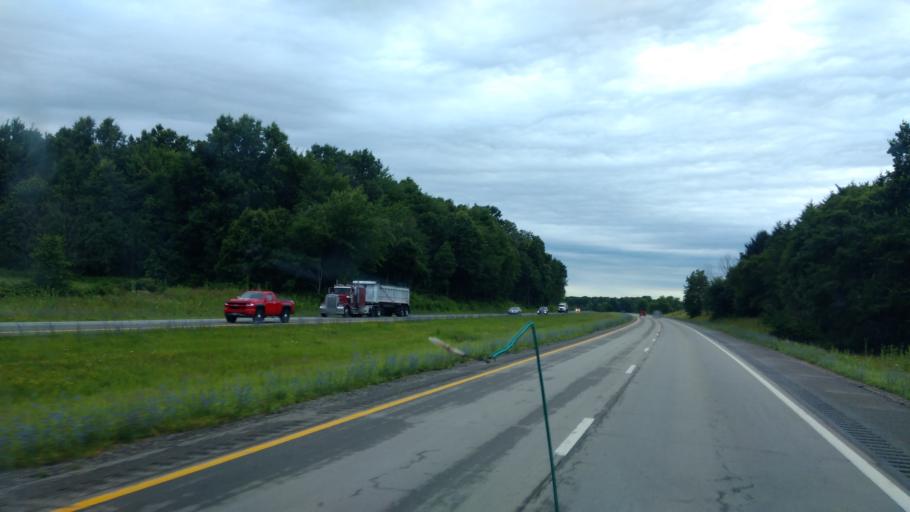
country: US
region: Ohio
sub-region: Columbiana County
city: Leetonia
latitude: 40.8443
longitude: -80.7321
